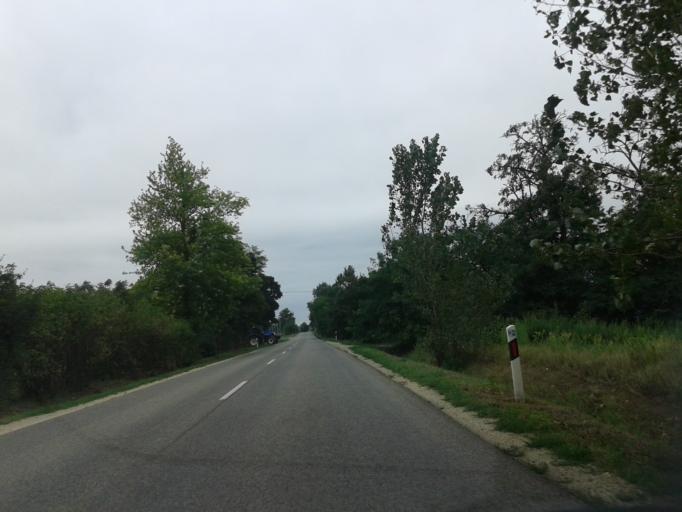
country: HU
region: Pest
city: Domsod
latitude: 47.0724
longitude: 19.0100
